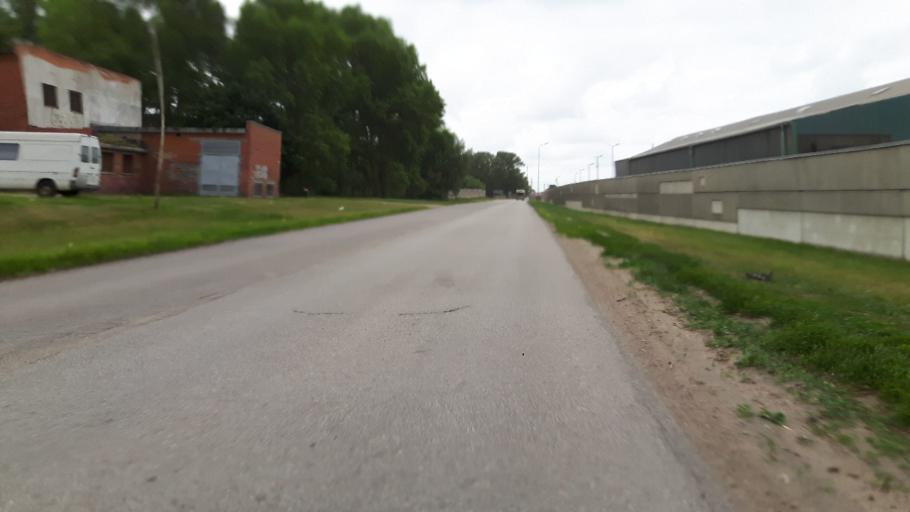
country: LV
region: Liepaja
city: Vec-Liepaja
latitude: 56.5351
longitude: 20.9993
